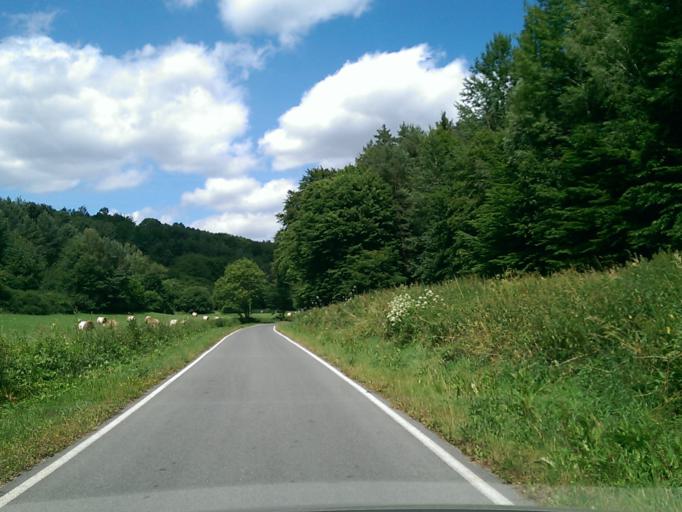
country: CZ
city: Duba
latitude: 50.4881
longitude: 14.5113
